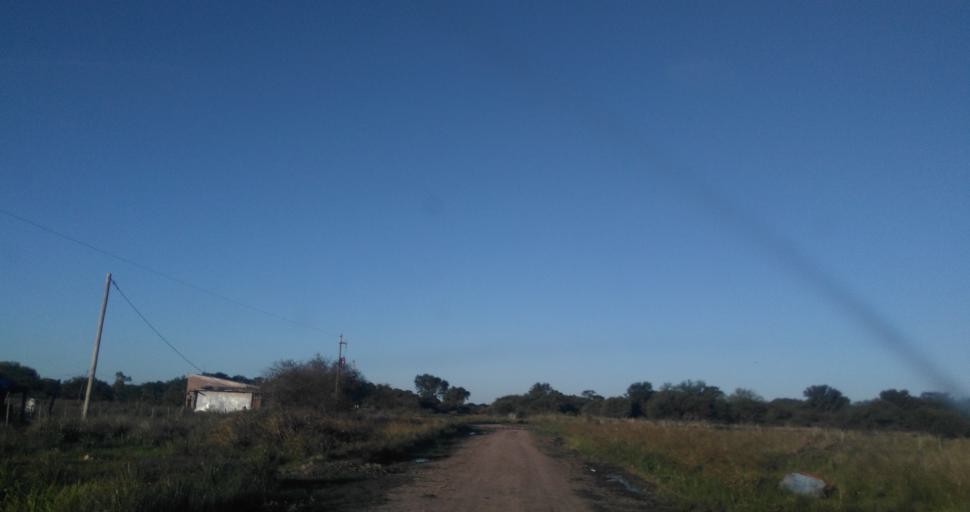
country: AR
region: Chaco
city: Fontana
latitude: -27.3870
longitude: -58.9741
